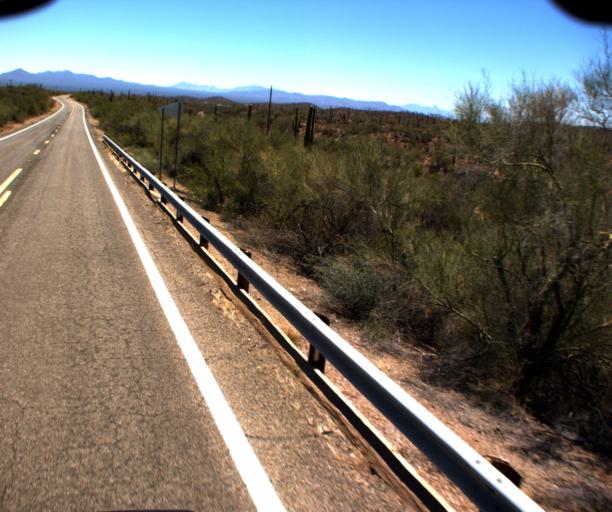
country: US
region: Arizona
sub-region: Pima County
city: Sells
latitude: 32.1695
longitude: -112.1414
